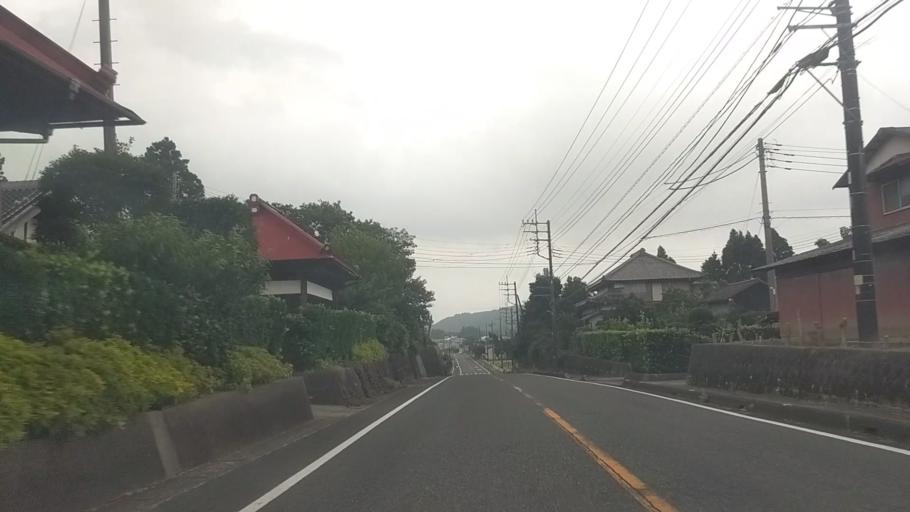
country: JP
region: Chiba
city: Ohara
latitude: 35.2819
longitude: 140.2934
